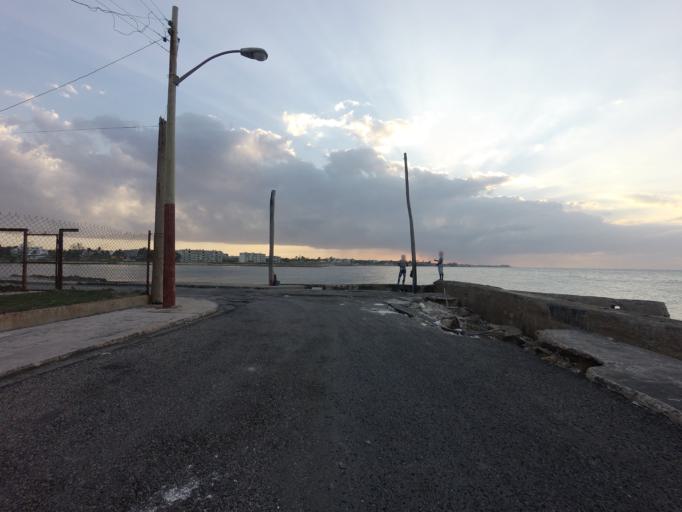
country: CU
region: La Habana
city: Cerro
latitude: 23.0954
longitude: -82.4617
